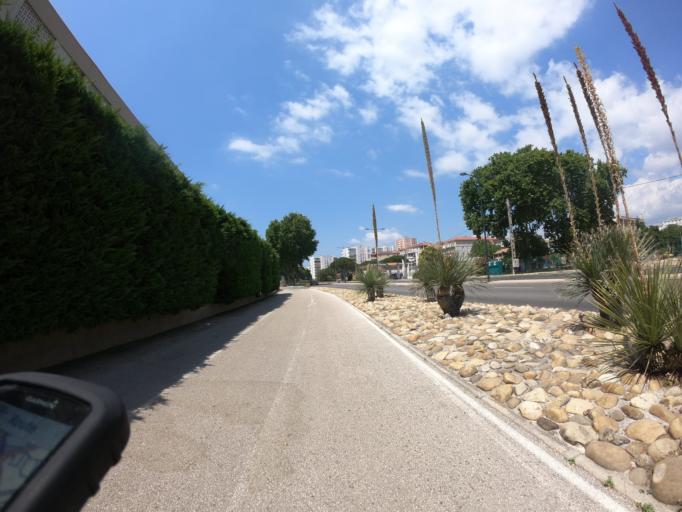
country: FR
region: Provence-Alpes-Cote d'Azur
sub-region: Departement du Var
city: La Seyne-sur-Mer
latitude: 43.1073
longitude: 5.8689
